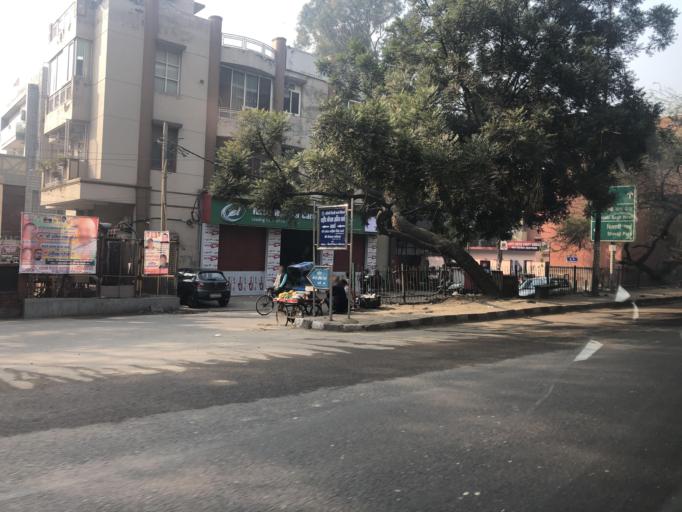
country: IN
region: NCT
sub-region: North West Delhi
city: Pitampura
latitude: 28.6747
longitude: 77.1314
